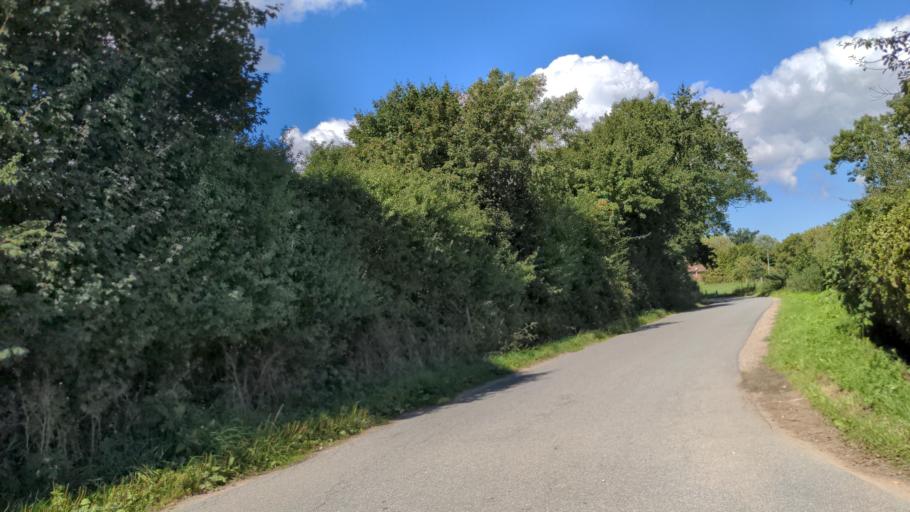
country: DE
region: Schleswig-Holstein
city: Beschendorf
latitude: 54.1759
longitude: 10.8449
